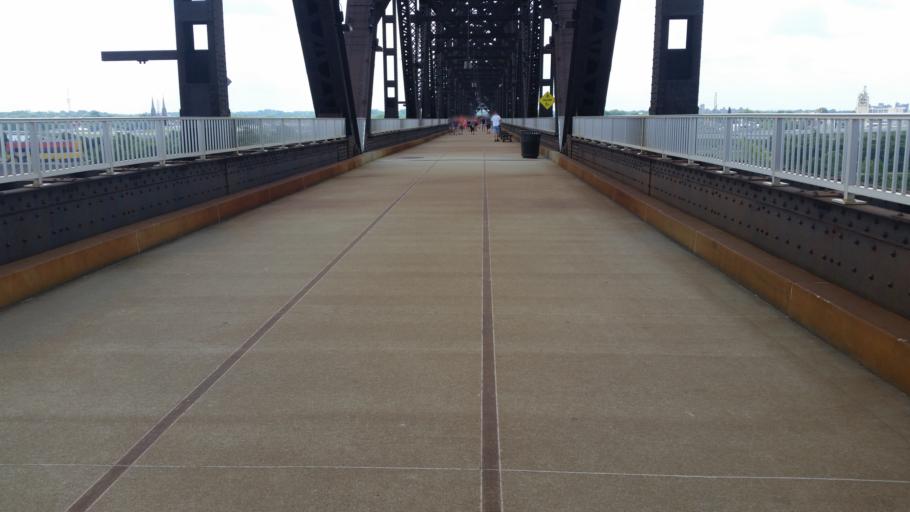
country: US
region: Indiana
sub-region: Clark County
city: Jeffersonville
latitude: 38.2654
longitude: -85.7390
